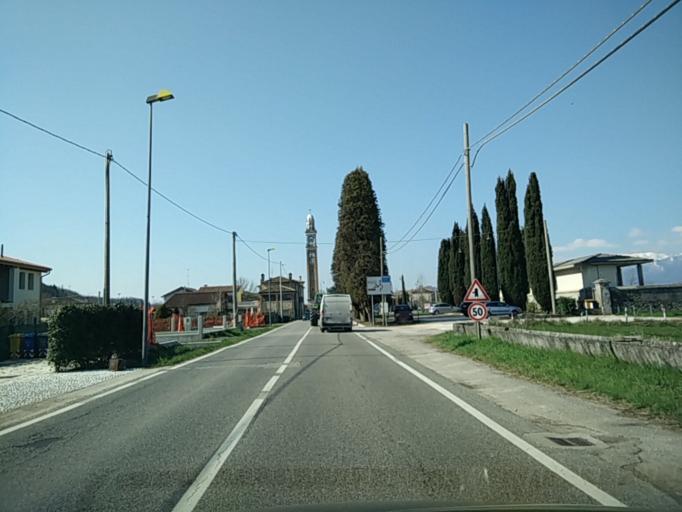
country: IT
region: Veneto
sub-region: Provincia di Treviso
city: Ciano
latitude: 45.8263
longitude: 12.0685
